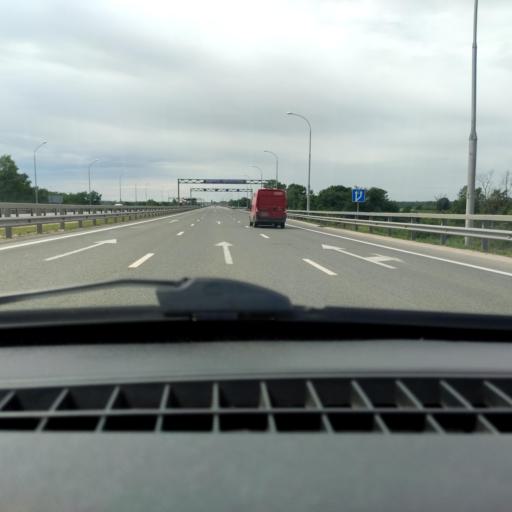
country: RU
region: Bashkortostan
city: Ufa
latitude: 54.6456
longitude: 55.9931
